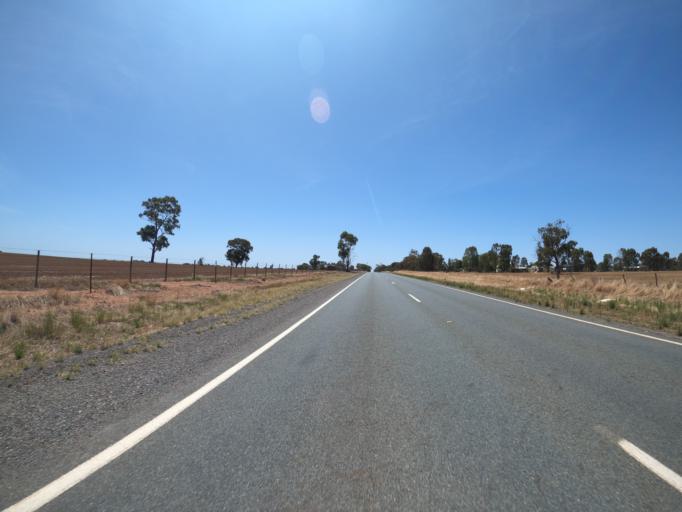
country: AU
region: Victoria
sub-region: Moira
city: Yarrawonga
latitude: -36.0508
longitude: 145.9955
